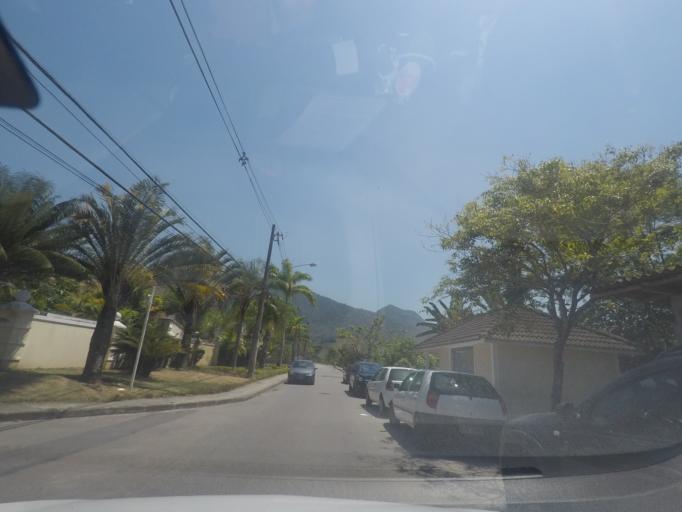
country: BR
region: Rio de Janeiro
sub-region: Nilopolis
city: Nilopolis
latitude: -22.9876
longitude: -43.4610
